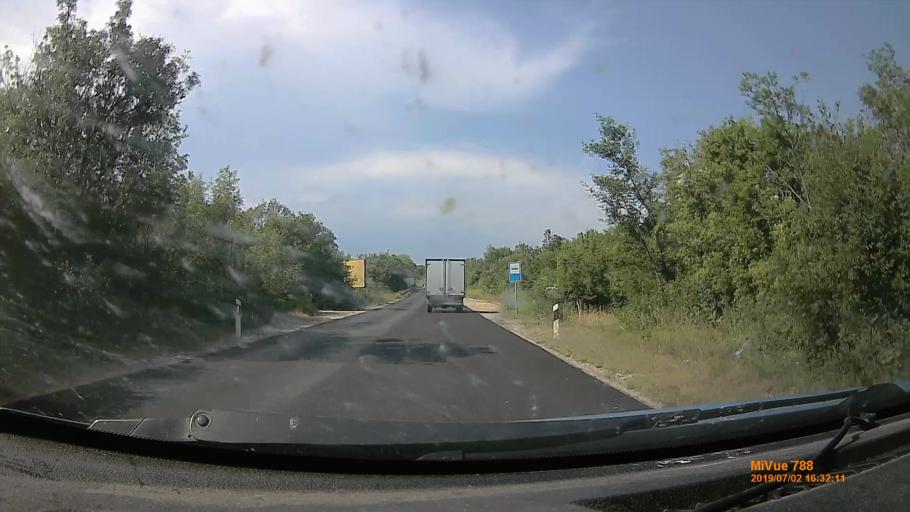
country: HR
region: Primorsko-Goranska
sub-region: Grad Krk
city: Krk
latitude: 45.0616
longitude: 14.4878
